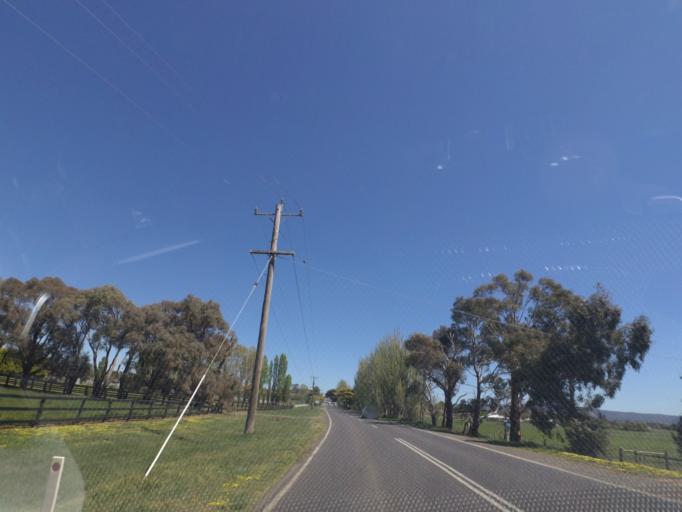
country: AU
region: Victoria
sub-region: Hume
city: Sunbury
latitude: -37.2775
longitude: 144.7441
